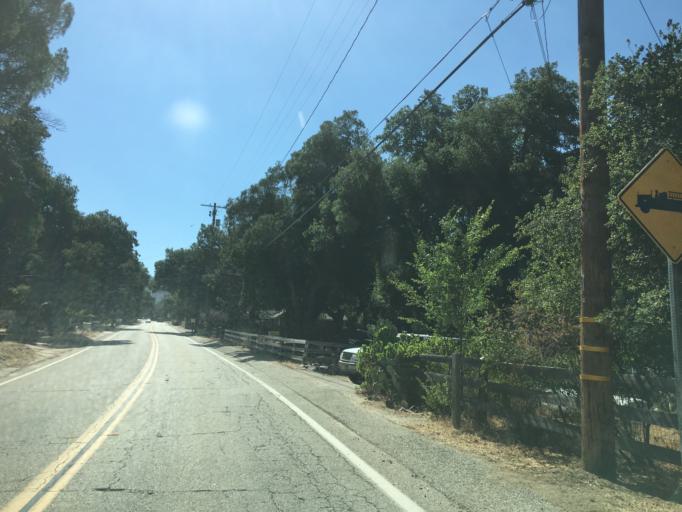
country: US
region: California
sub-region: Los Angeles County
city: Green Valley
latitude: 34.6181
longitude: -118.4116
